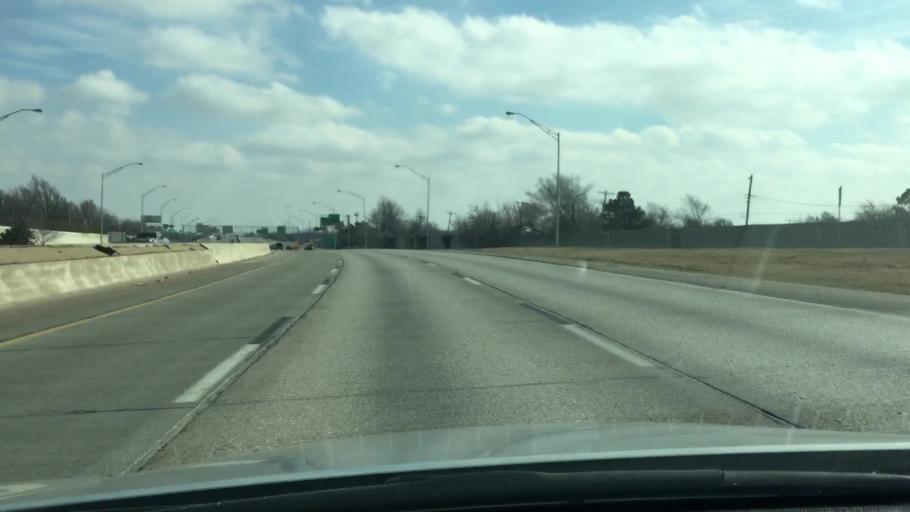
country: US
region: Oklahoma
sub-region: Oklahoma County
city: Oklahoma City
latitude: 35.3955
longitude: -97.5730
